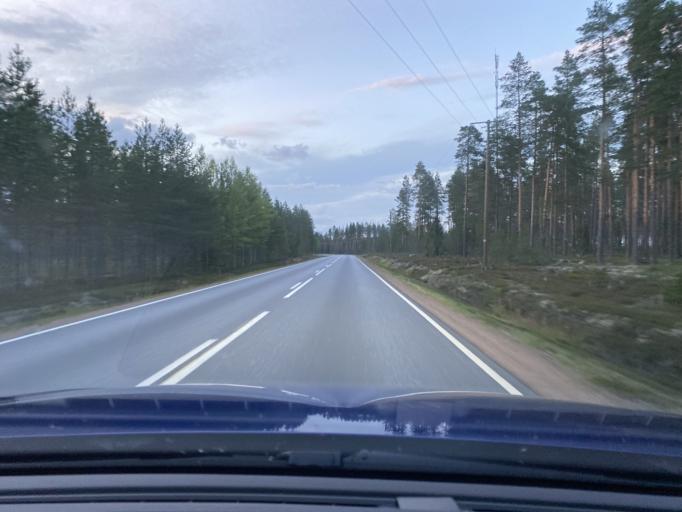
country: FI
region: Satakunta
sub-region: Pohjois-Satakunta
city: Honkajoki
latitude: 62.1902
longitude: 22.2974
